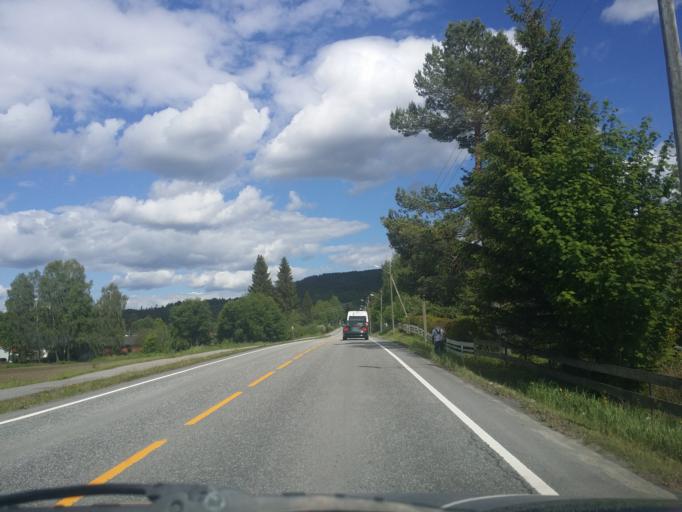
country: NO
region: Oppland
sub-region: Jevnaker
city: Jevnaker
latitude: 60.2412
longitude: 10.4133
